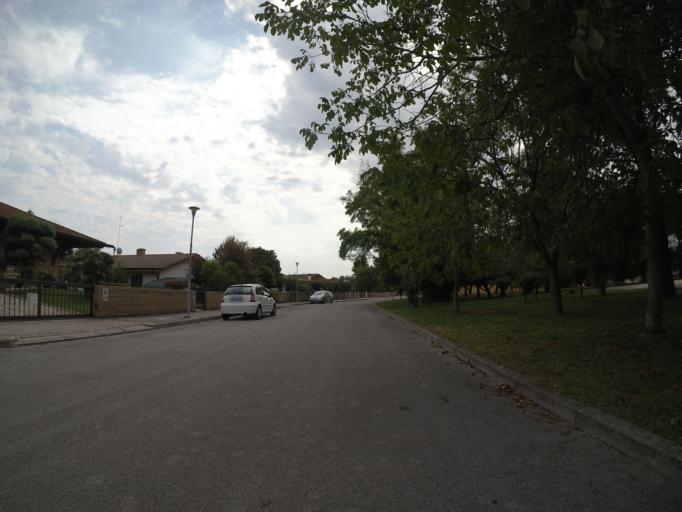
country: IT
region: Friuli Venezia Giulia
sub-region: Provincia di Udine
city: Codroipo
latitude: 45.9564
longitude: 12.9983
